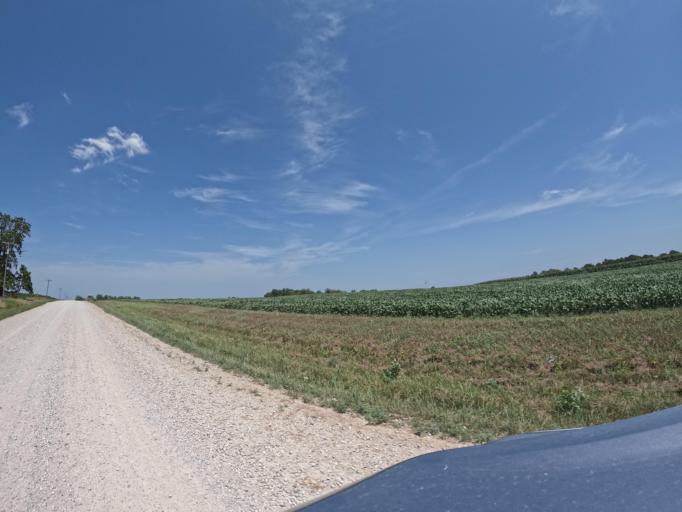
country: US
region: Iowa
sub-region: Henry County
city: Mount Pleasant
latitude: 40.9365
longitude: -91.6457
